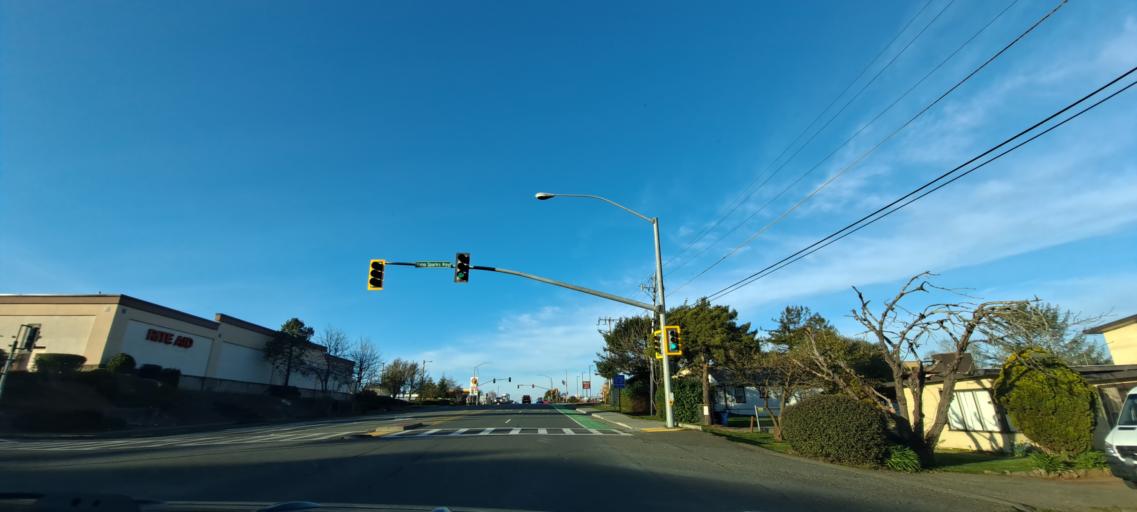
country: US
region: California
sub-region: Humboldt County
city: McKinleyville
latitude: 40.9327
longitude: -124.1008
